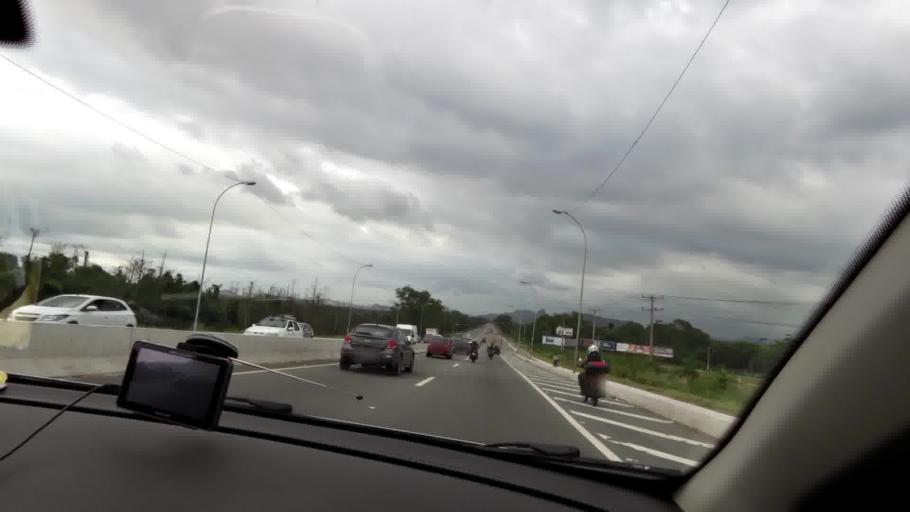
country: BR
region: Espirito Santo
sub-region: Vila Velha
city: Vila Velha
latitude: -20.2392
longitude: -40.2792
